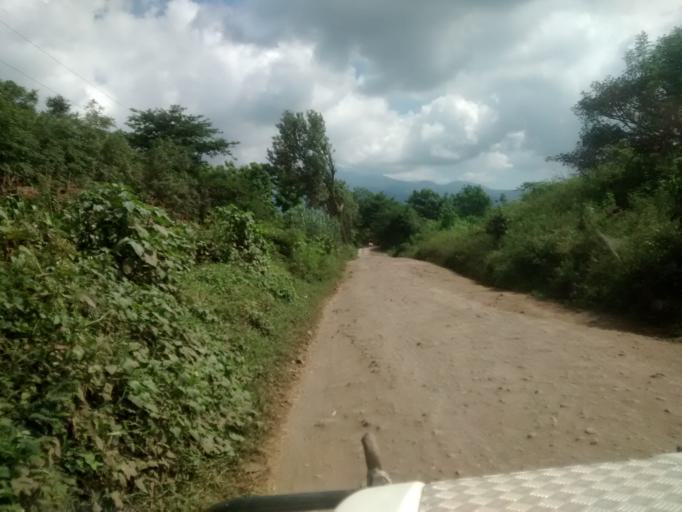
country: TZ
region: Arusha
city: Usa River
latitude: -3.3630
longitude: 36.8437
